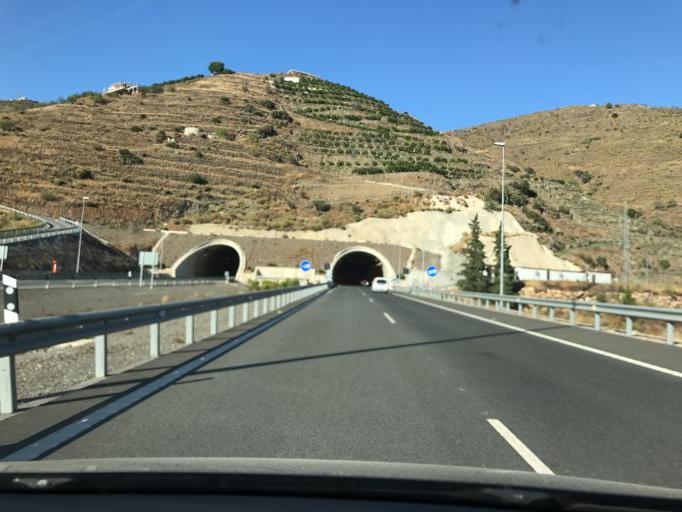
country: ES
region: Andalusia
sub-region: Provincia de Granada
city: Itrabo
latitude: 36.7625
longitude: -3.6456
